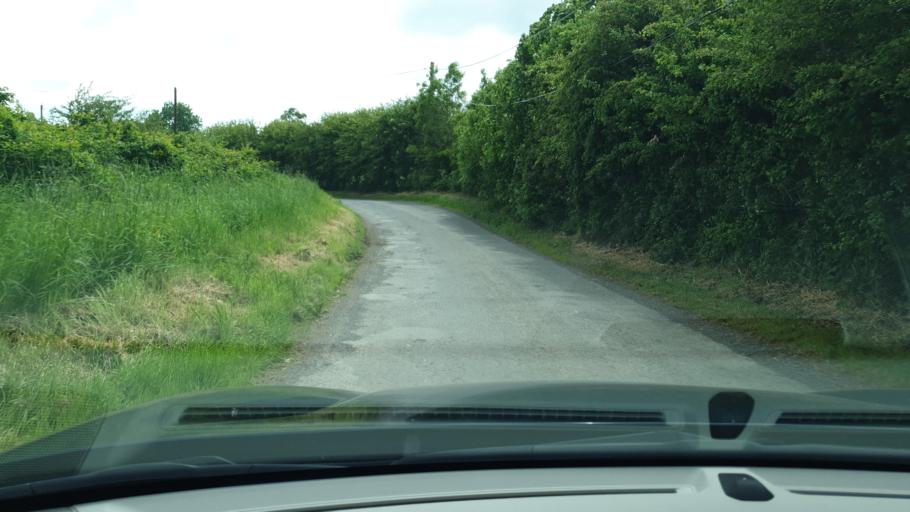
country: IE
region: Ulster
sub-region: An Cabhan
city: Kingscourt
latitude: 53.7986
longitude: -6.7226
